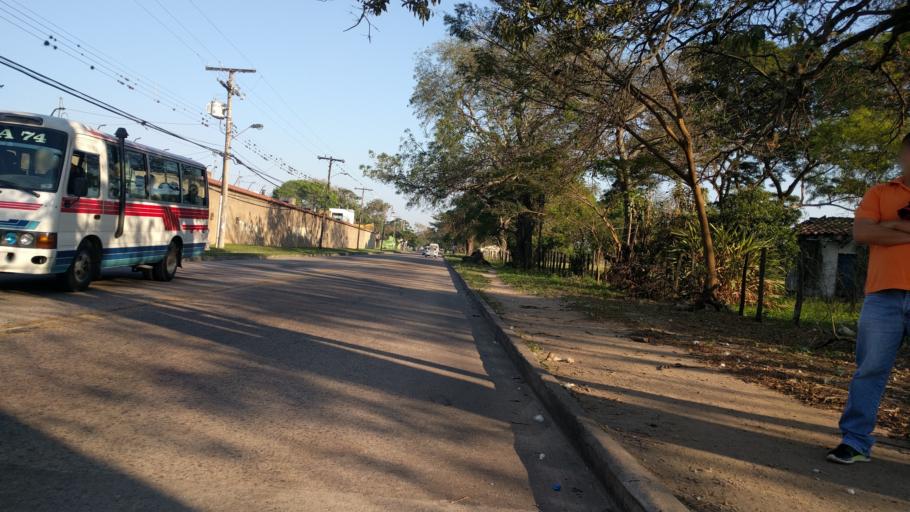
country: BO
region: Santa Cruz
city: Santa Cruz de la Sierra
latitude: -17.8129
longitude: -63.1635
